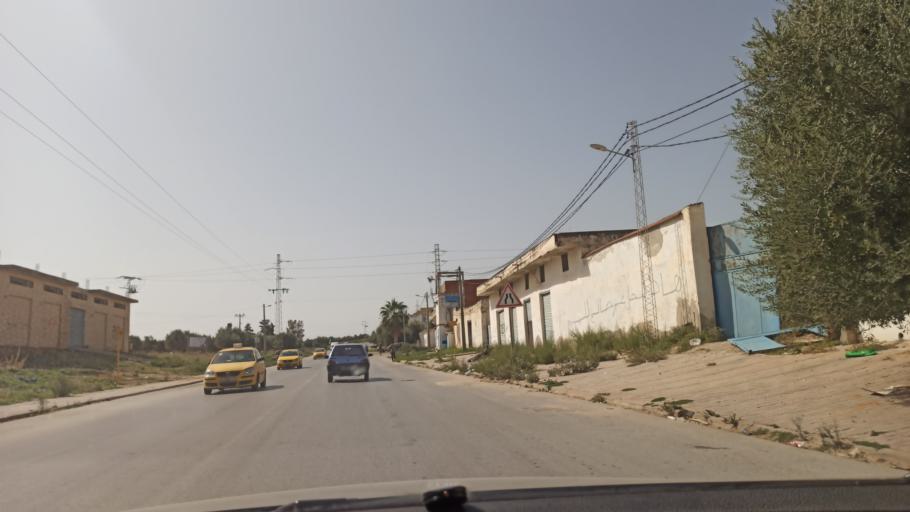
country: TN
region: Manouba
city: Manouba
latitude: 36.7515
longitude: 10.1005
